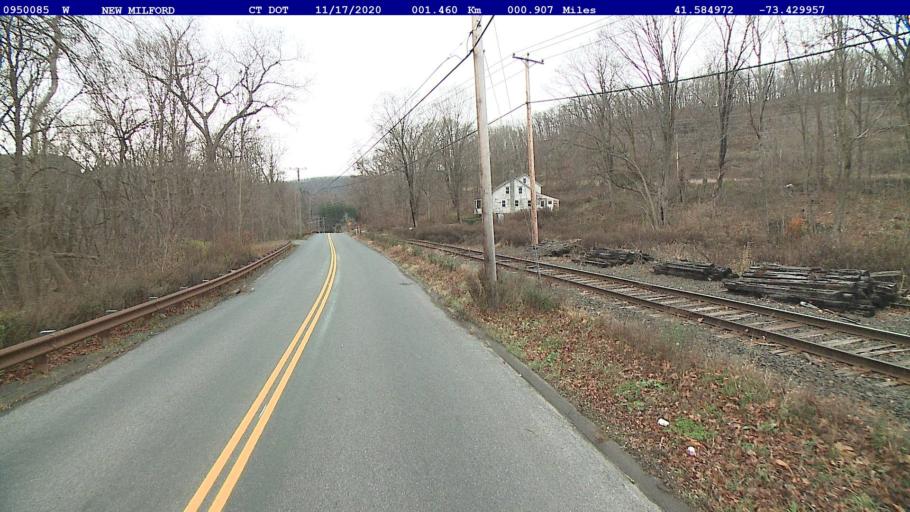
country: US
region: Connecticut
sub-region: Litchfield County
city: New Milford
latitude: 41.5850
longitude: -73.4300
